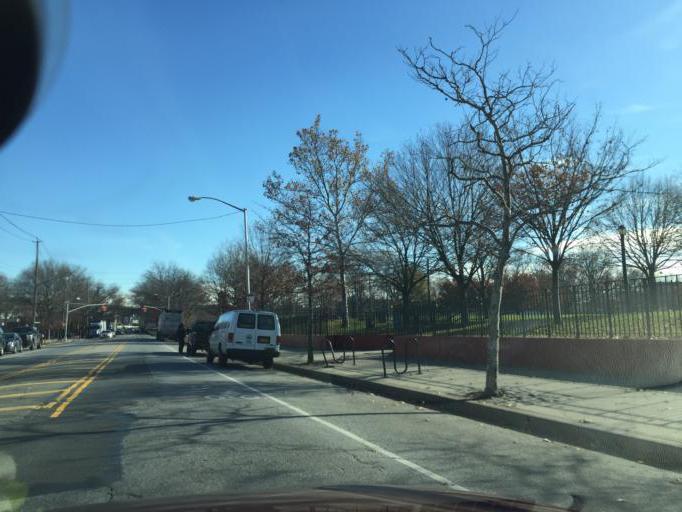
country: US
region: New York
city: New York City
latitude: 40.6722
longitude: -74.0046
